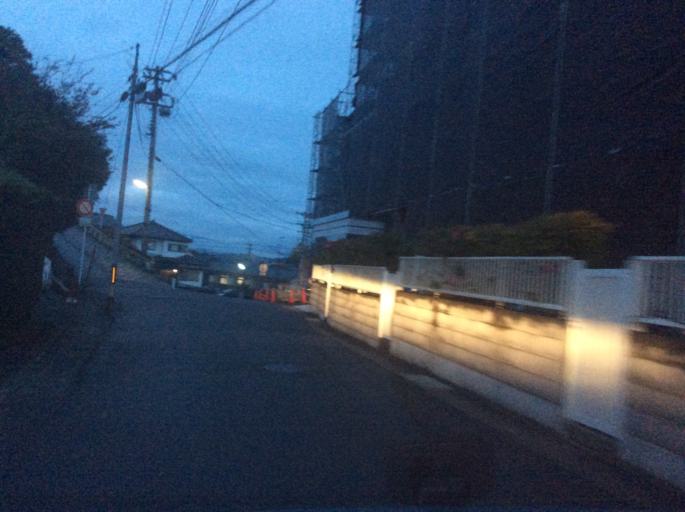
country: JP
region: Fukushima
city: Iwaki
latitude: 37.0615
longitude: 140.8915
